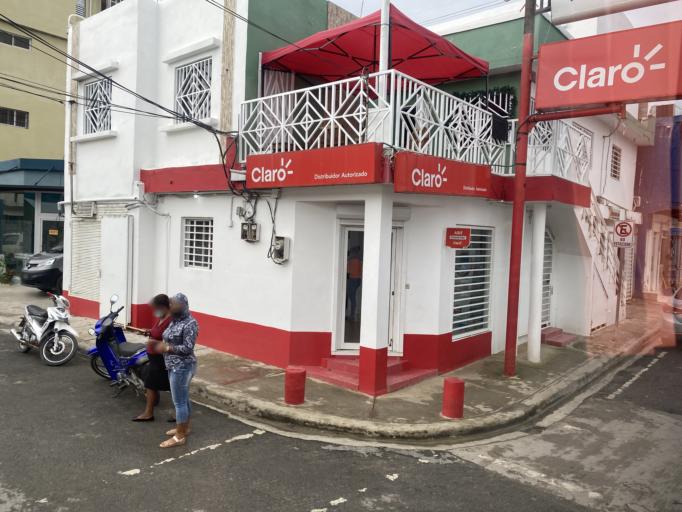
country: DO
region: El Seibo
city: Miches
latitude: 18.9842
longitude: -69.0476
